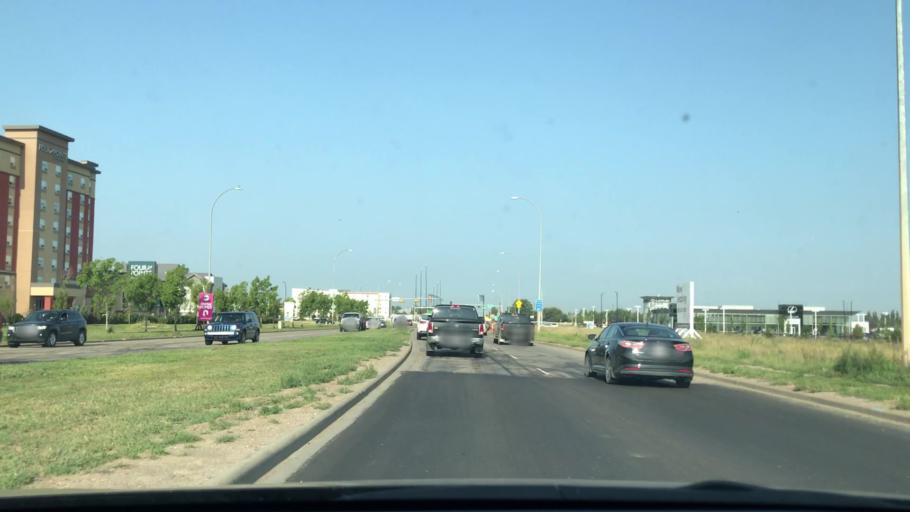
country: CA
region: Alberta
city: Beaumont
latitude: 53.4249
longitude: -113.4858
